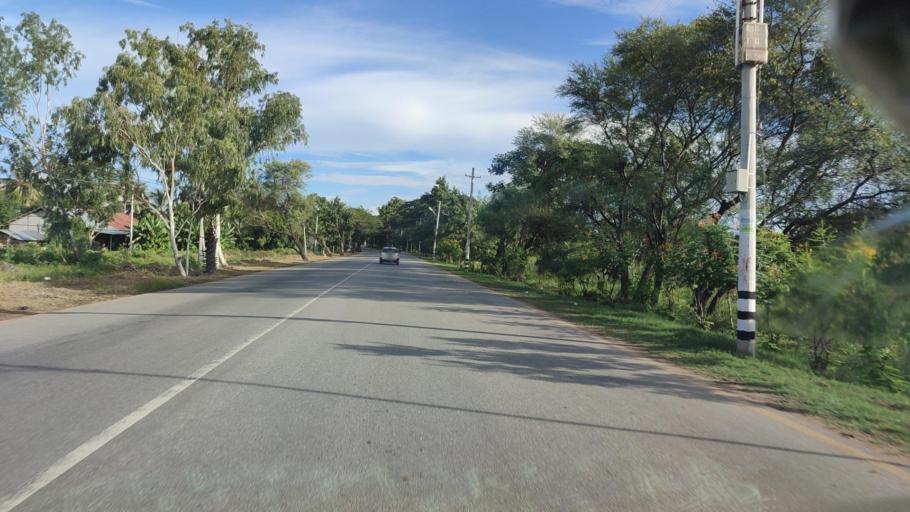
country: MM
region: Mandalay
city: Yamethin
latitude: 20.1461
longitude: 96.1939
